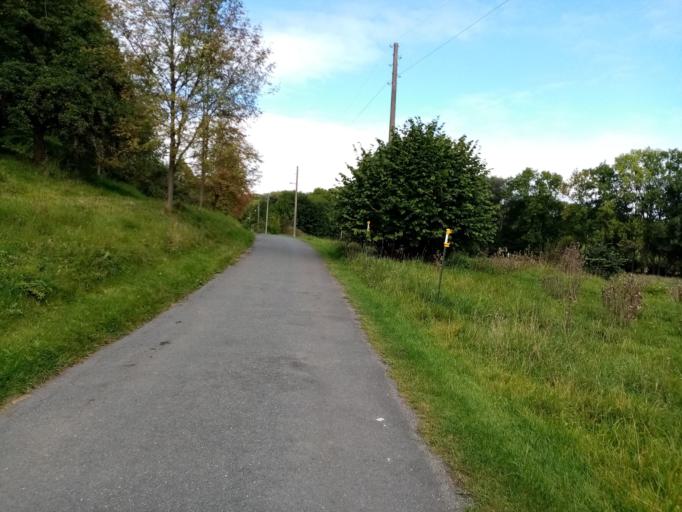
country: DE
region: Thuringia
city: Dingelstadt
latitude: 51.3149
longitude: 10.3029
